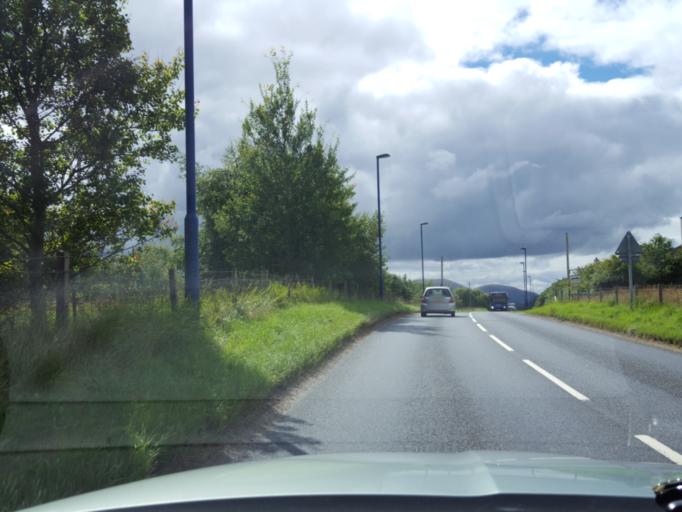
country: GB
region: Scotland
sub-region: Highland
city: Aviemore
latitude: 57.2041
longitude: -3.8268
